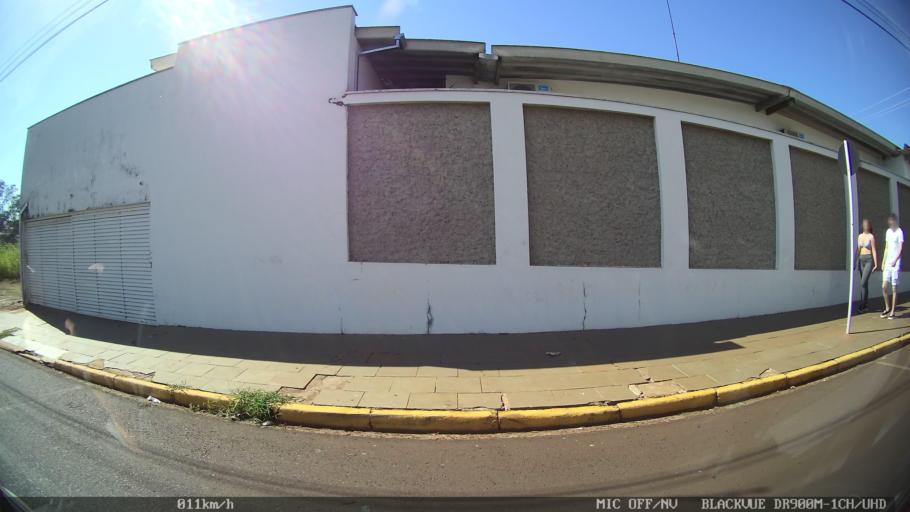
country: BR
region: Sao Paulo
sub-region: Batatais
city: Batatais
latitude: -20.8885
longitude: -47.5828
